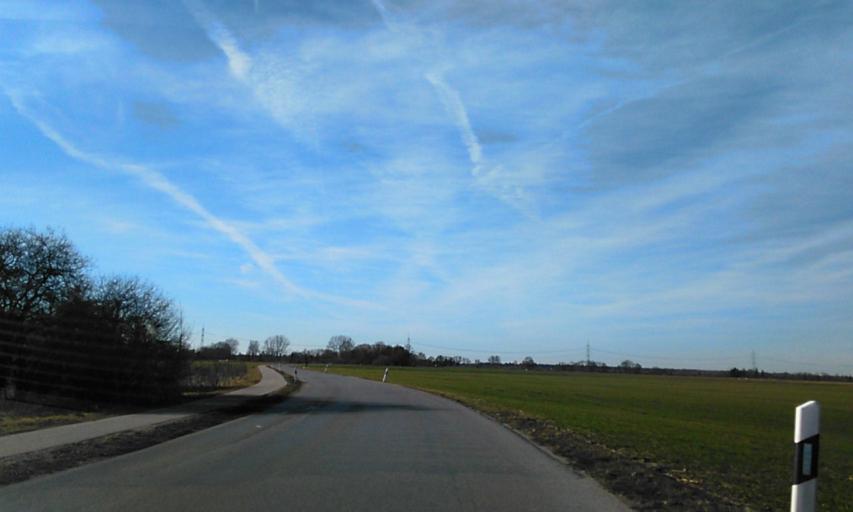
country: DE
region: Bavaria
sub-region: Swabia
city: Brunnen
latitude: 48.2505
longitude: 10.9604
